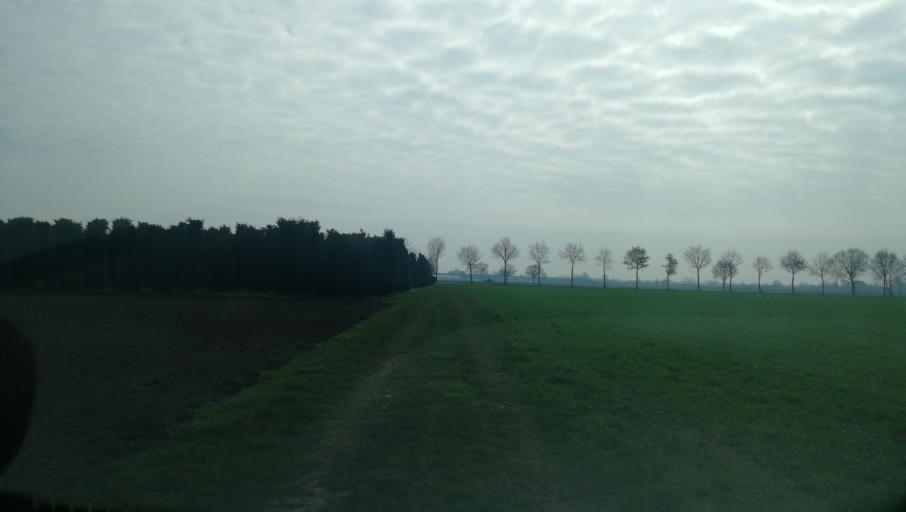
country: NL
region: Limburg
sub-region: Gemeente Peel en Maas
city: Maasbree
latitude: 51.4288
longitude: 6.0596
